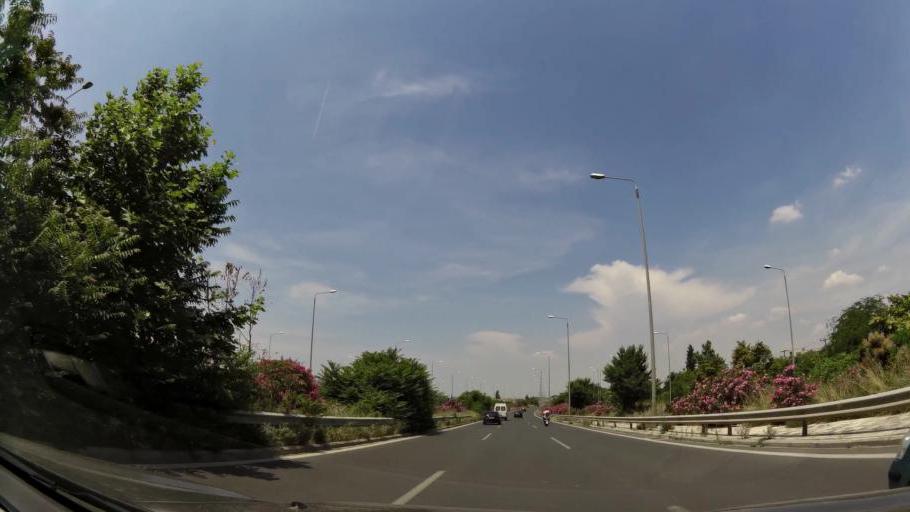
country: GR
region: Central Macedonia
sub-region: Nomos Thessalonikis
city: Menemeni
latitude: 40.6497
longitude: 22.9079
